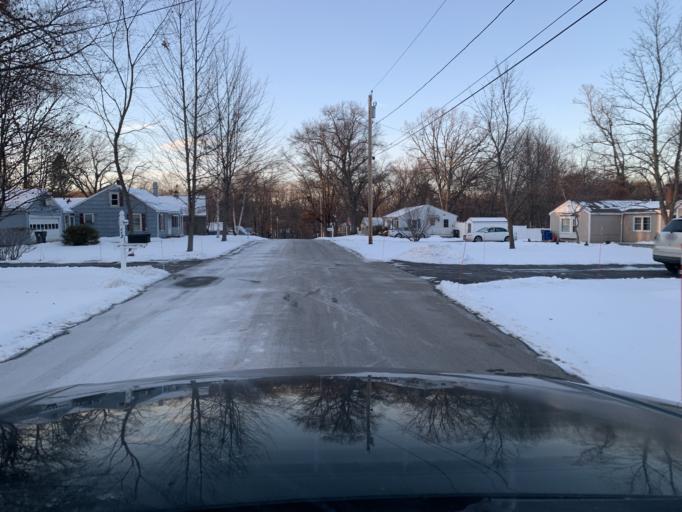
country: US
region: Massachusetts
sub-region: Essex County
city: Haverhill
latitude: 42.7910
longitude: -71.1122
